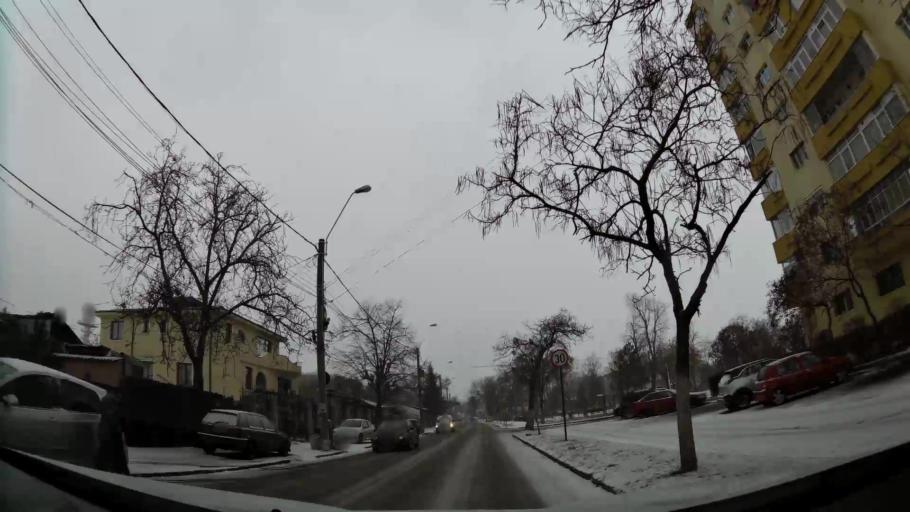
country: RO
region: Prahova
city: Ploiesti
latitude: 44.9305
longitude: 26.0083
